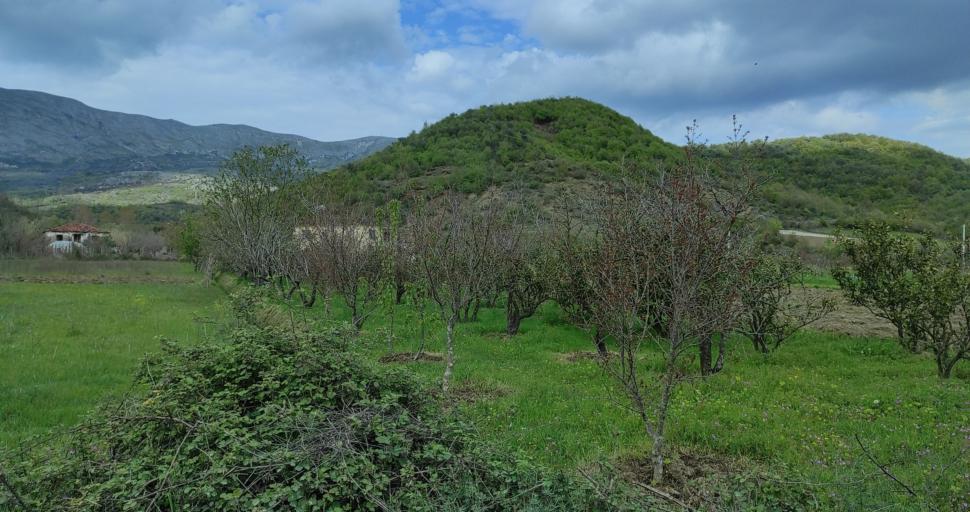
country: AL
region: Shkoder
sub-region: Rrethi i Shkodres
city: Dajc
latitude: 42.0276
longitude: 19.4189
